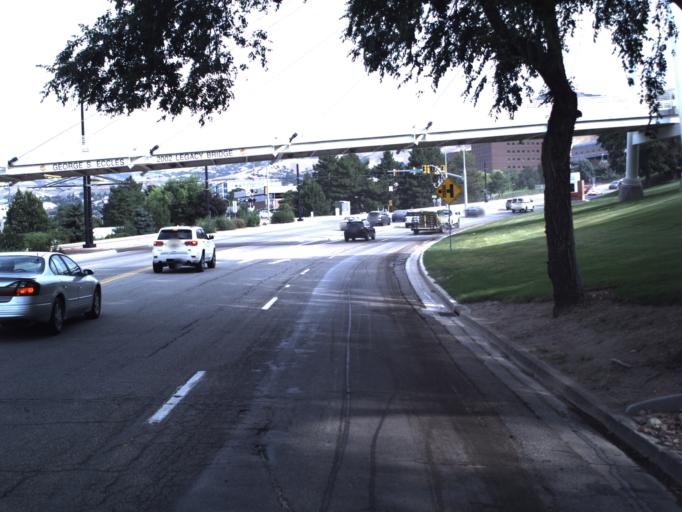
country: US
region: Utah
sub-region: Salt Lake County
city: Salt Lake City
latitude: 40.7647
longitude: -111.8365
